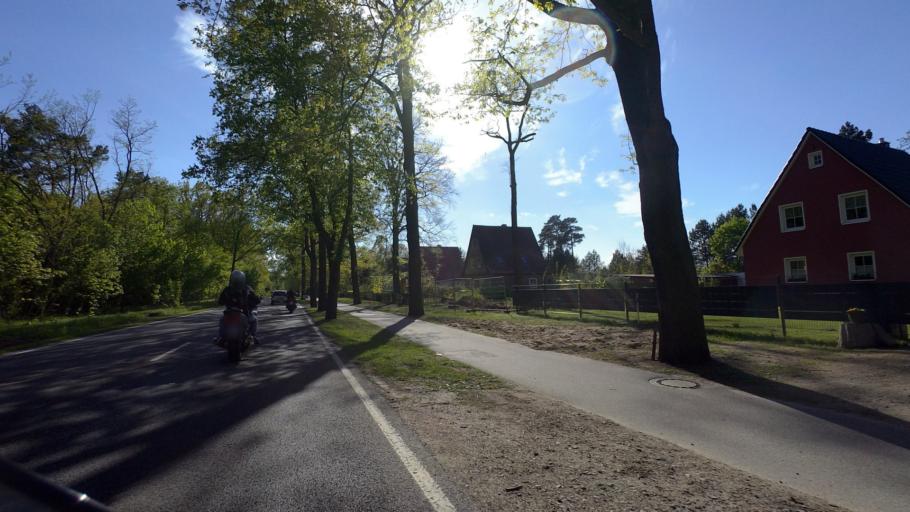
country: DE
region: Brandenburg
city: Oranienburg
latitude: 52.7641
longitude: 13.2739
